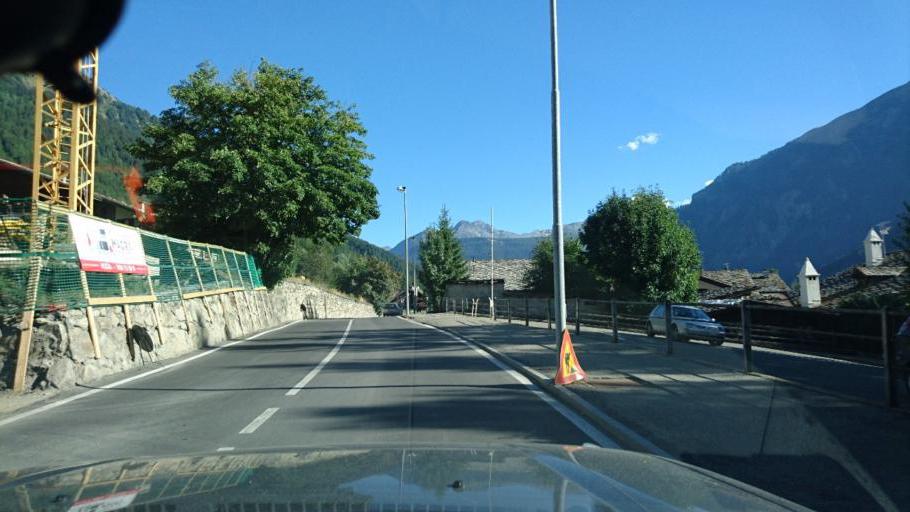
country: IT
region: Aosta Valley
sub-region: Valle d'Aosta
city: Courmayeur
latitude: 45.7975
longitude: 6.9695
